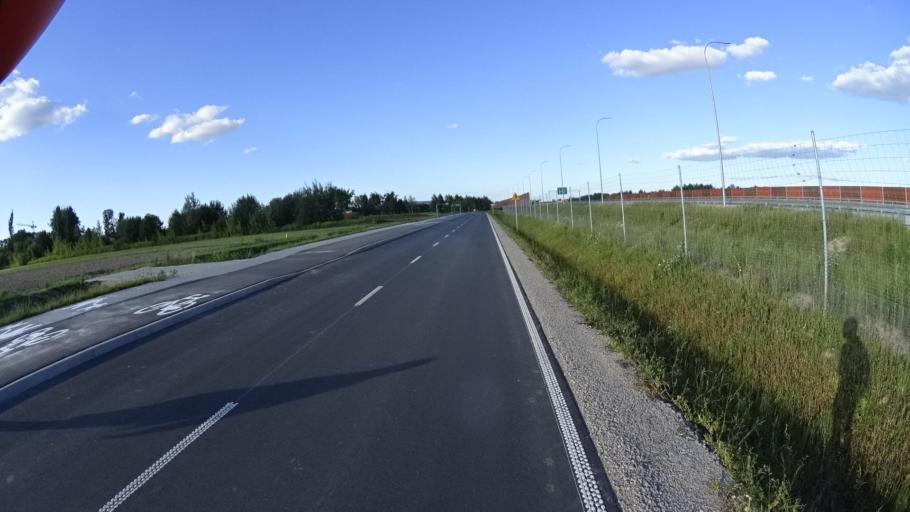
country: PL
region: Masovian Voivodeship
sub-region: Powiat piaseczynski
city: Mysiadlo
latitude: 52.1100
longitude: 20.9764
